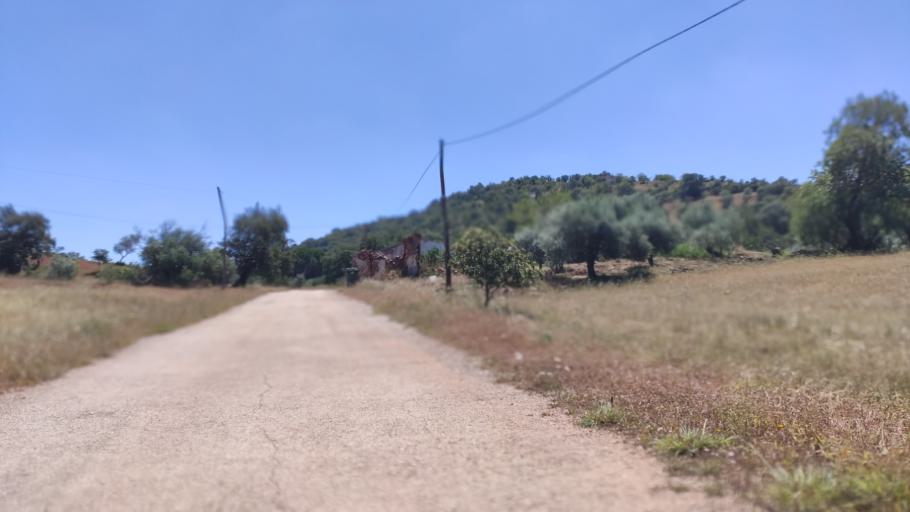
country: PT
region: Faro
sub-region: Sao Bras de Alportel
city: Sao Bras de Alportel
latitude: 37.1739
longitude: -7.9245
